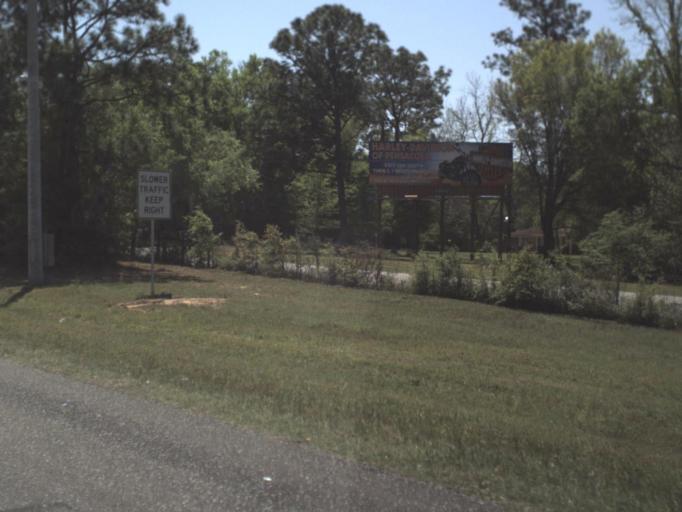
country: US
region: Florida
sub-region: Escambia County
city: Ensley
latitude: 30.5117
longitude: -87.2956
